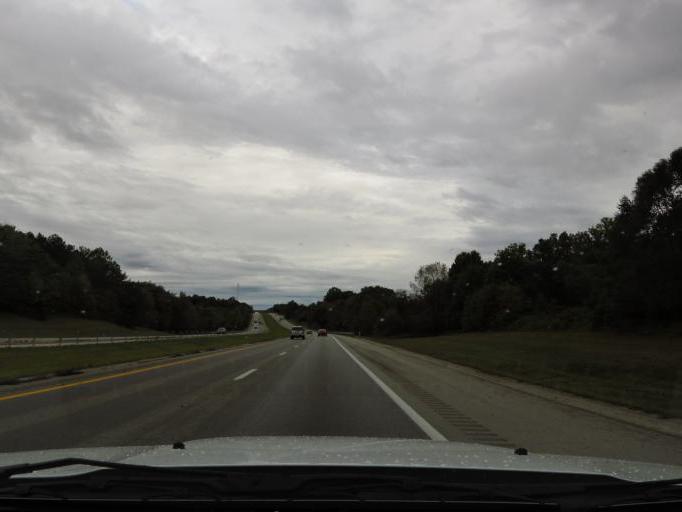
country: US
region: Kentucky
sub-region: Laurel County
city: London
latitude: 37.1790
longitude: -84.1330
